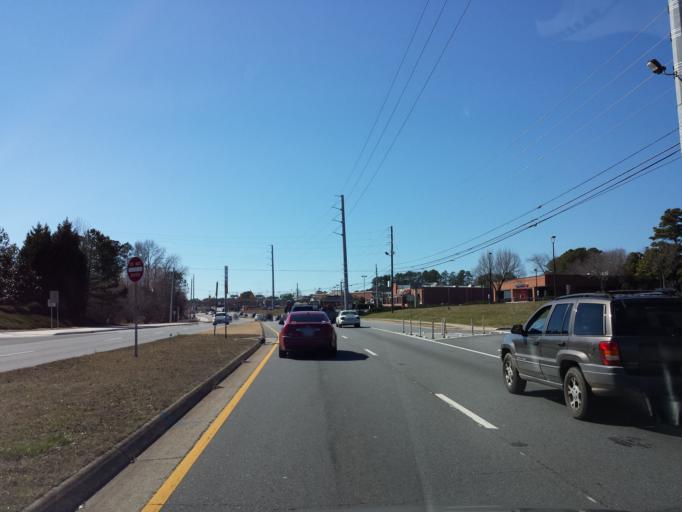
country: US
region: Georgia
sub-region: Cobb County
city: Kennesaw
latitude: 33.9537
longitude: -84.6517
